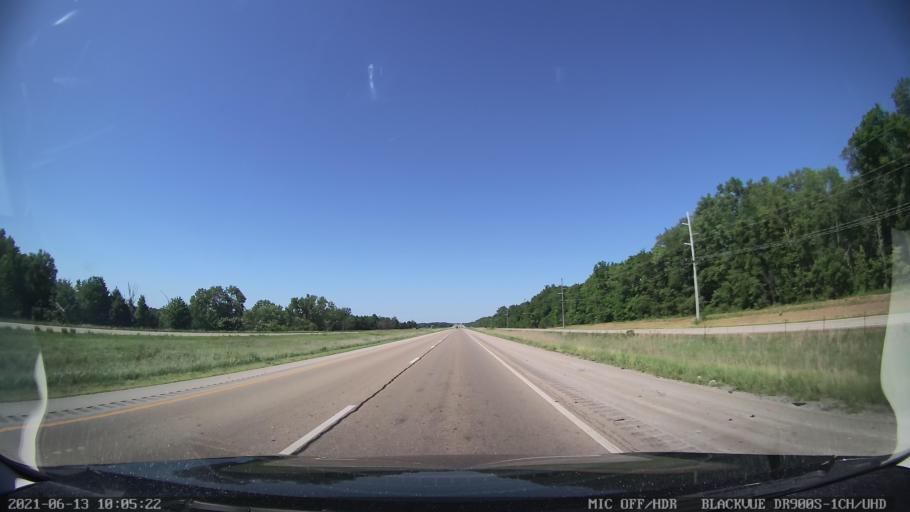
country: US
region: Illinois
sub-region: Logan County
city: Atlanta
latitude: 40.2427
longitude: -89.2535
